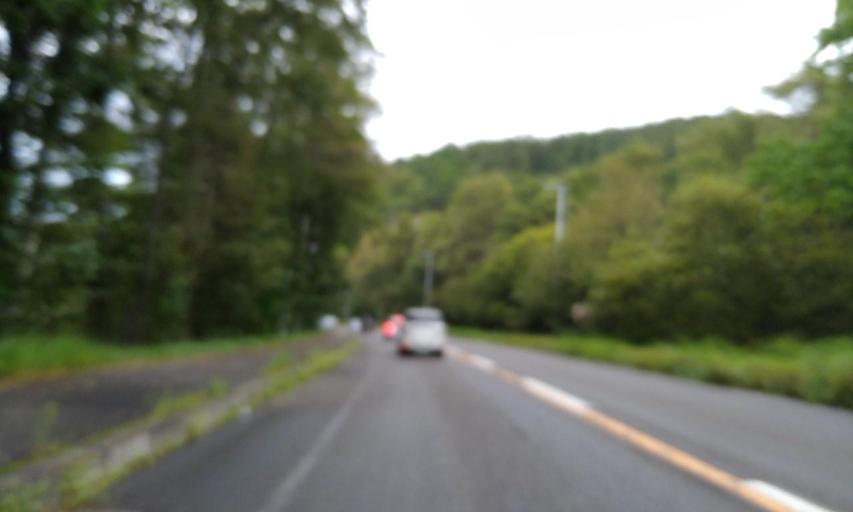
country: JP
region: Hokkaido
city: Abashiri
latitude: 43.9733
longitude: 144.2179
